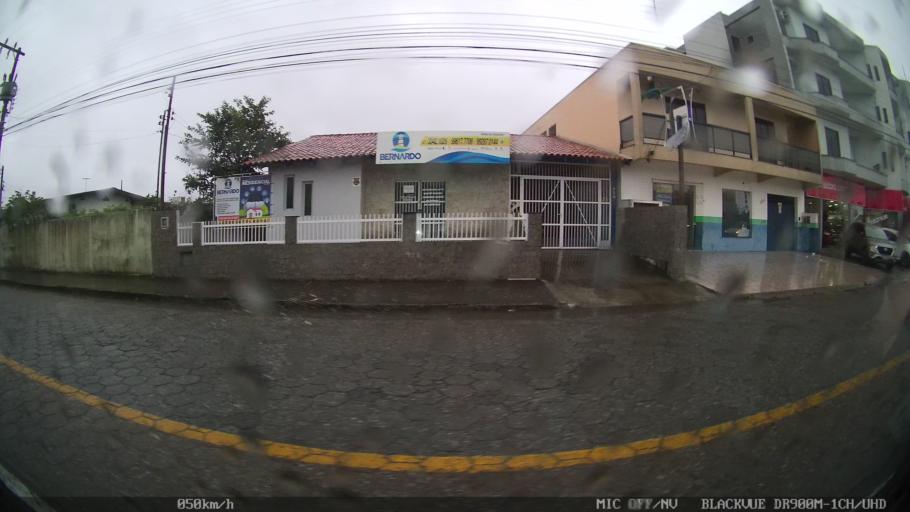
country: BR
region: Santa Catarina
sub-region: Navegantes
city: Navegantes
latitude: -26.8959
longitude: -48.6524
